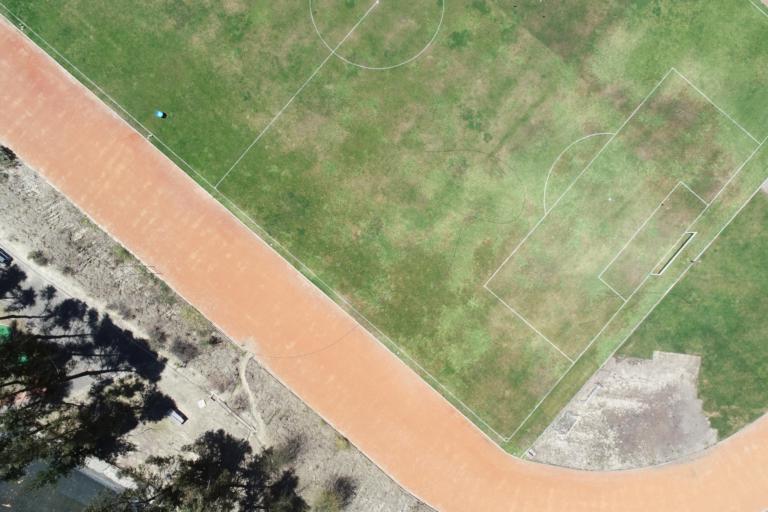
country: BO
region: La Paz
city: La Paz
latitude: -16.6273
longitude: -68.0582
